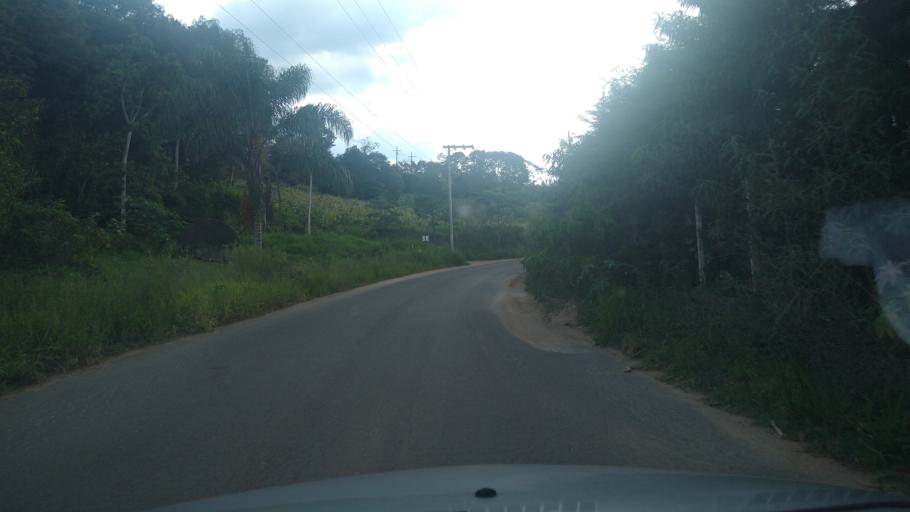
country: BR
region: Minas Gerais
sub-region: Extrema
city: Extrema
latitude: -22.7207
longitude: -46.3413
